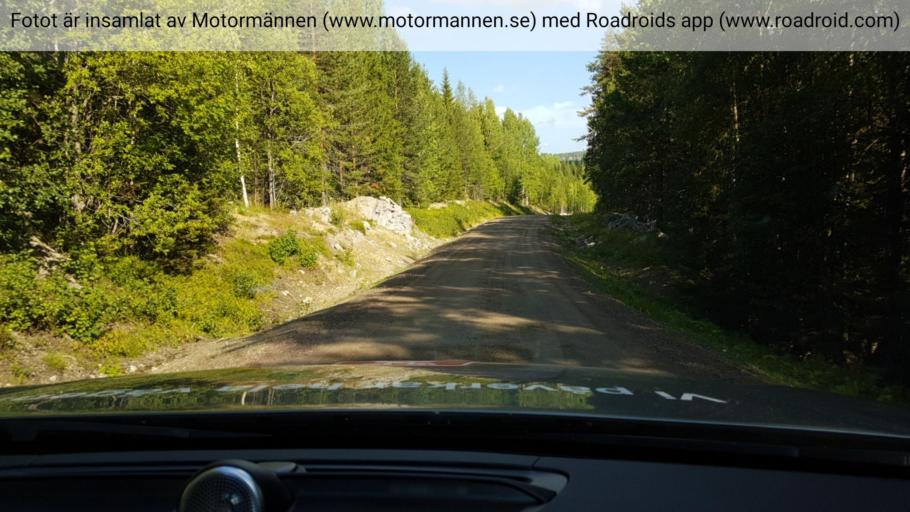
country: SE
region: Vaesterbotten
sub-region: Dorotea Kommun
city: Dorotea
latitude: 63.9821
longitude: 16.0240
